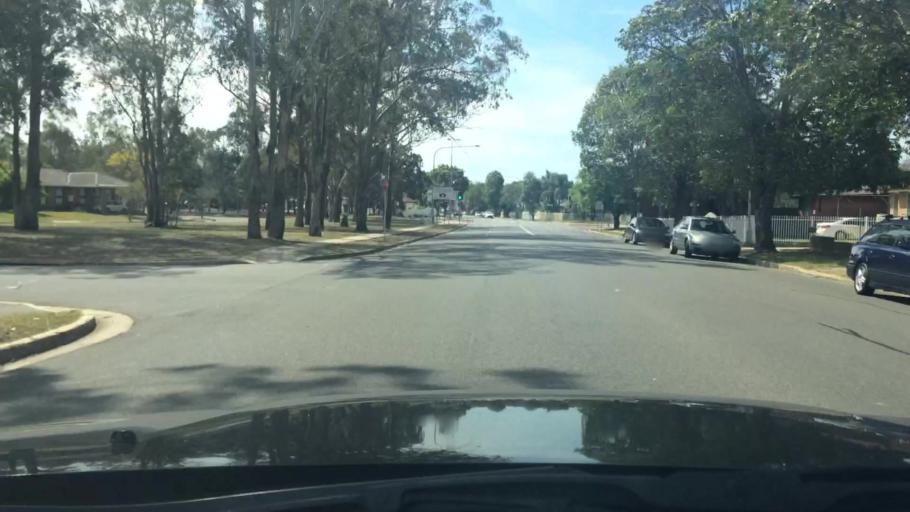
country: AU
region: New South Wales
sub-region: Fairfield
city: Cabramatta West
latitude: -33.8665
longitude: 150.8956
